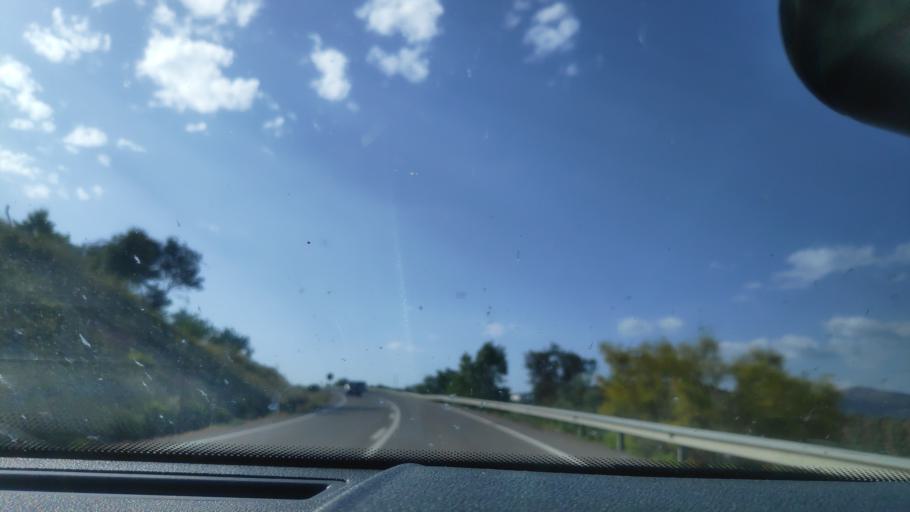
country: ES
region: Andalusia
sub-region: Provincia de Jaen
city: Frailes
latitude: 37.4494
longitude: -3.8682
